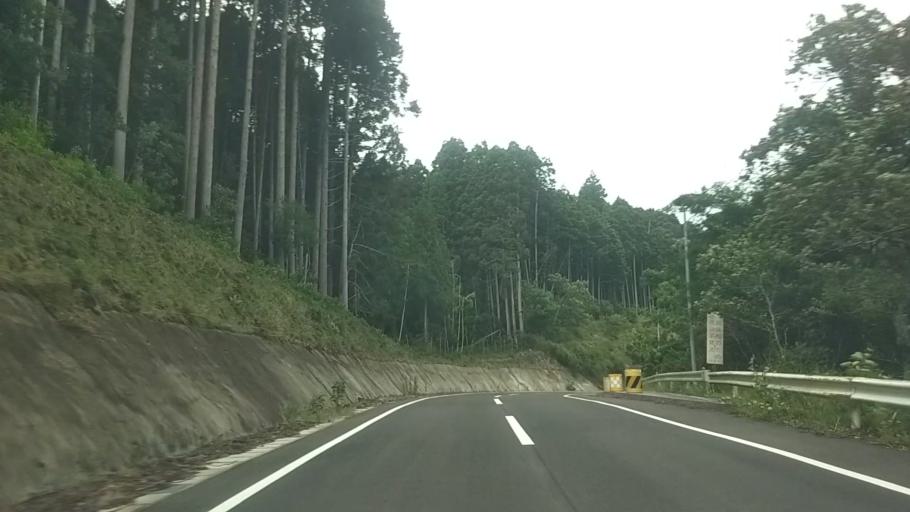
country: JP
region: Chiba
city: Kawaguchi
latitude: 35.1876
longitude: 140.1383
